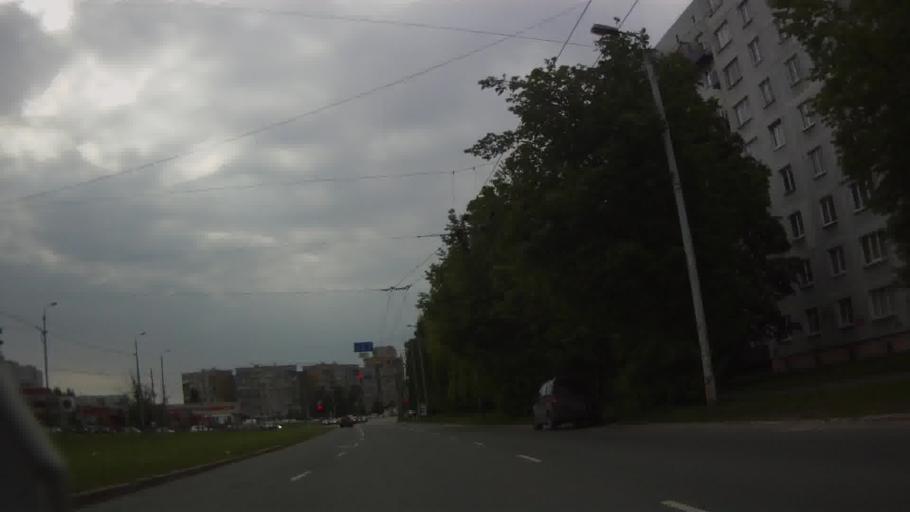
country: LV
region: Riga
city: Riga
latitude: 56.9592
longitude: 24.1798
